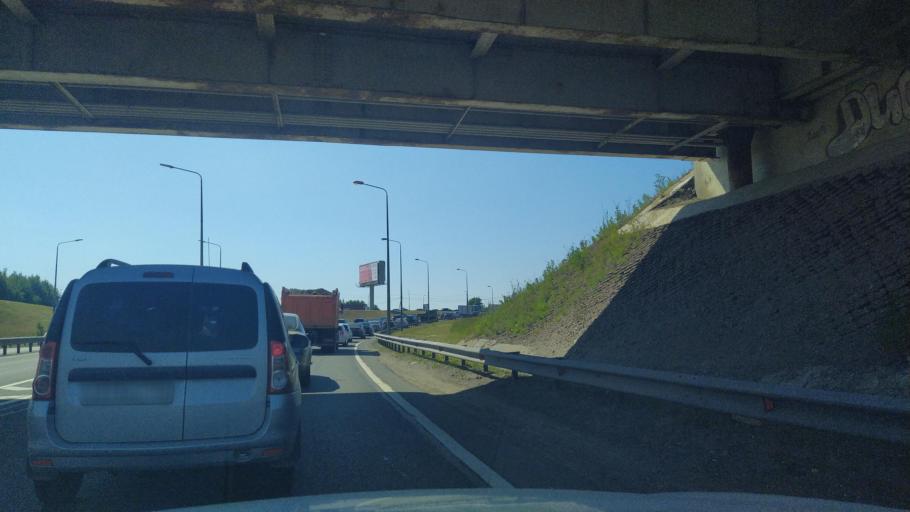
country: RU
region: St.-Petersburg
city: Pargolovo
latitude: 60.1005
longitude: 30.2553
